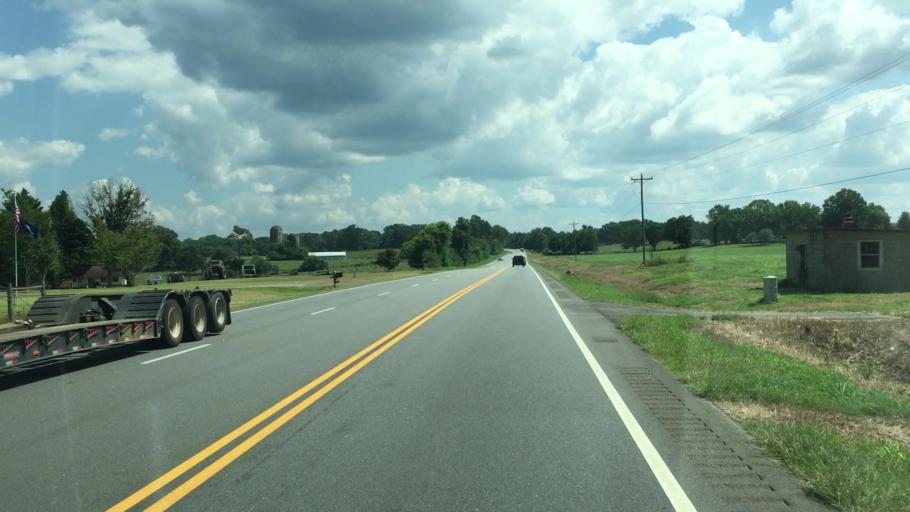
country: US
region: Georgia
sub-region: Morgan County
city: Madison
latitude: 33.4827
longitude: -83.4356
